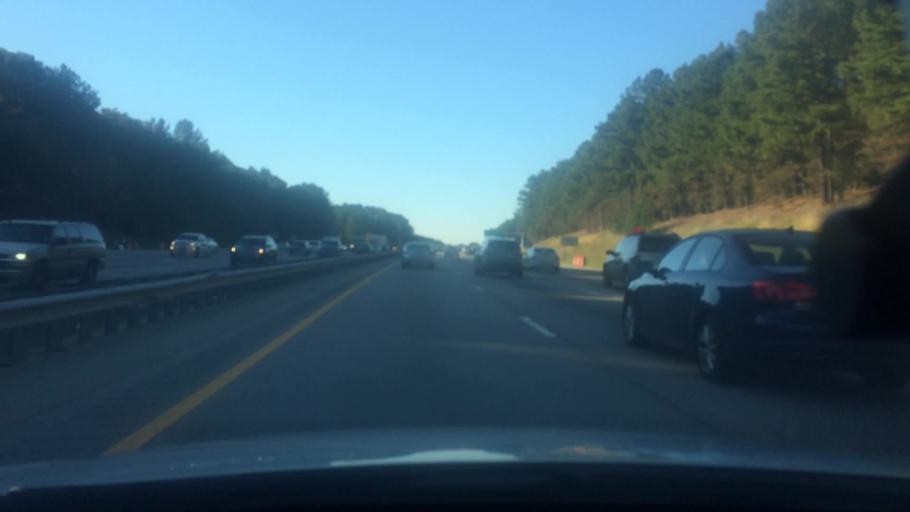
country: US
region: North Carolina
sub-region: Wake County
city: Morrisville
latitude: 35.8463
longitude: -78.7925
